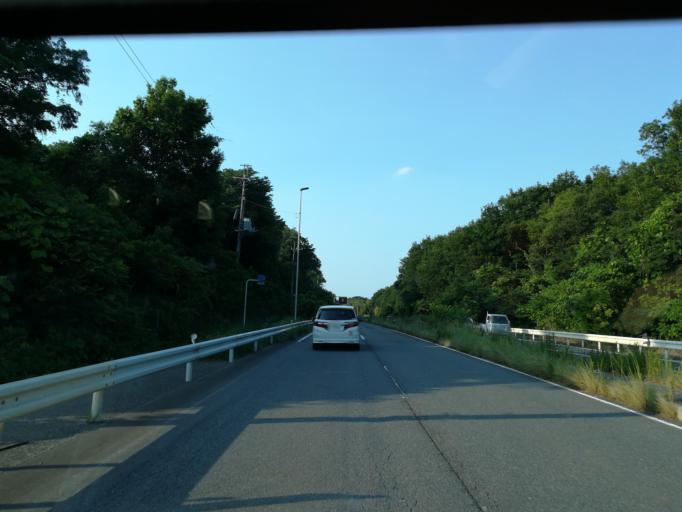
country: JP
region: Saitama
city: Kumagaya
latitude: 36.1074
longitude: 139.3685
